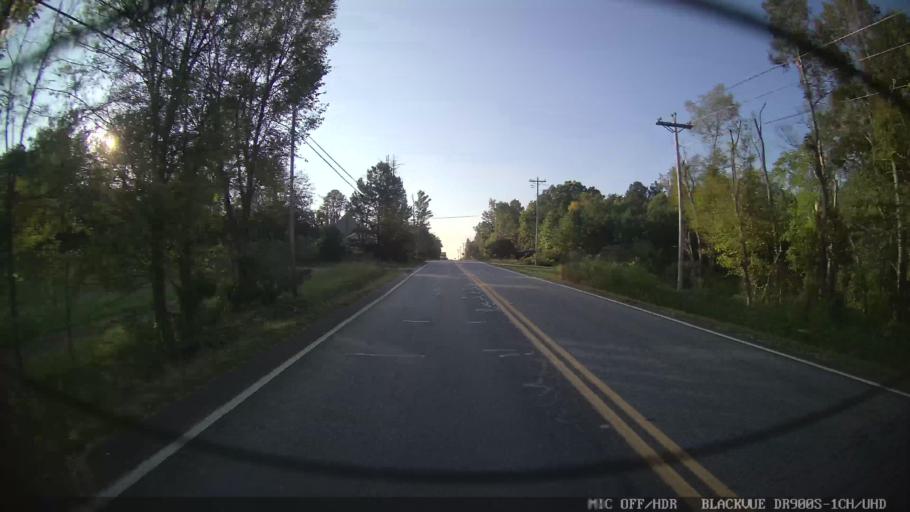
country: US
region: Tennessee
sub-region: Bradley County
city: Wildwood Lake
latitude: 34.9812
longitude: -84.7333
